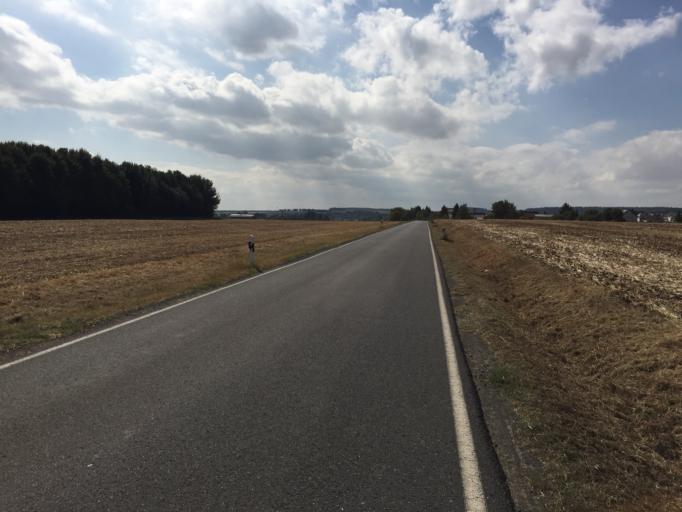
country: DE
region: Hesse
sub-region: Regierungsbezirk Giessen
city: Hungen
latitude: 50.4492
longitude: 8.8524
